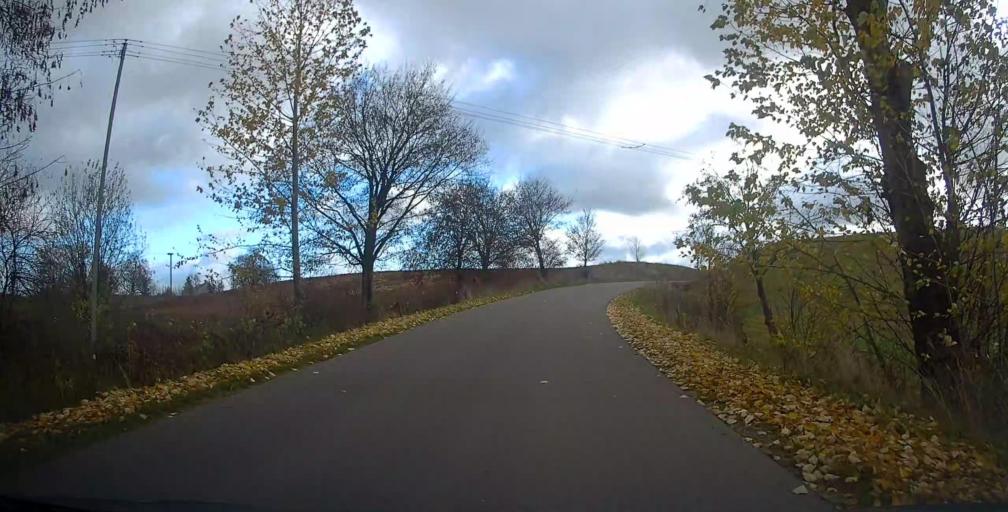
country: PL
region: Podlasie
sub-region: Suwalki
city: Suwalki
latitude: 54.3422
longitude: 22.8594
